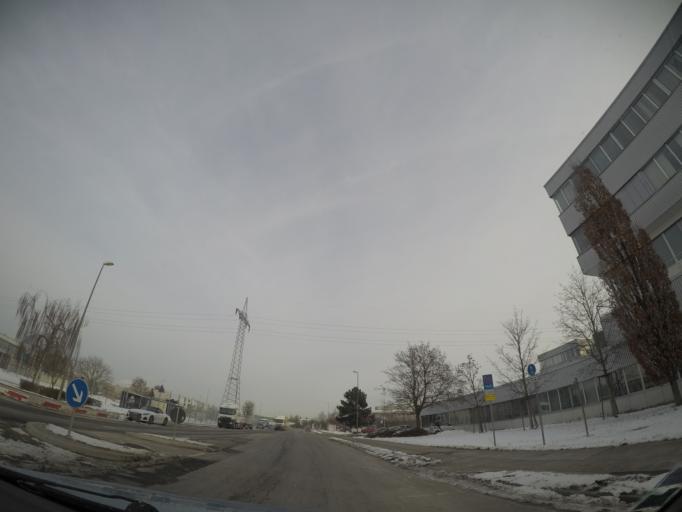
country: DE
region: Bavaria
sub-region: Swabia
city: Neu-Ulm
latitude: 48.3887
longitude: 10.0363
